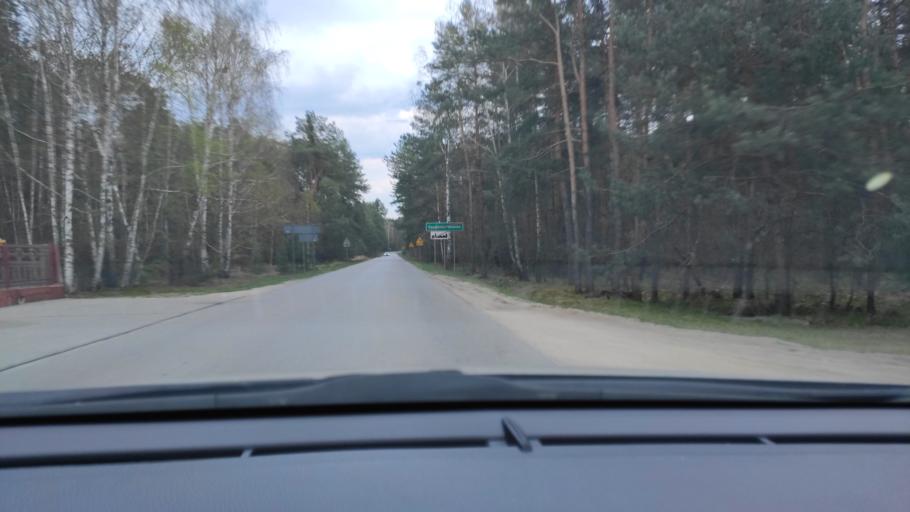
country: PL
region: Masovian Voivodeship
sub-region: Powiat radomski
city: Pionki
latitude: 51.5494
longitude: 21.3697
